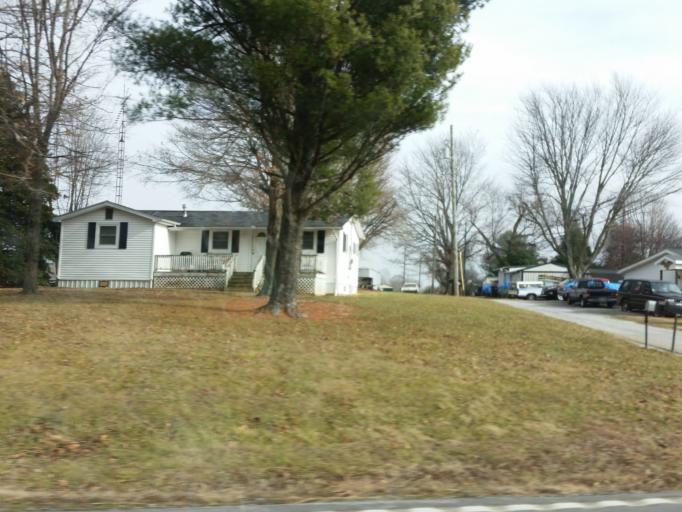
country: US
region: Indiana
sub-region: Jefferson County
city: Madison
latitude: 38.6847
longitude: -85.3279
